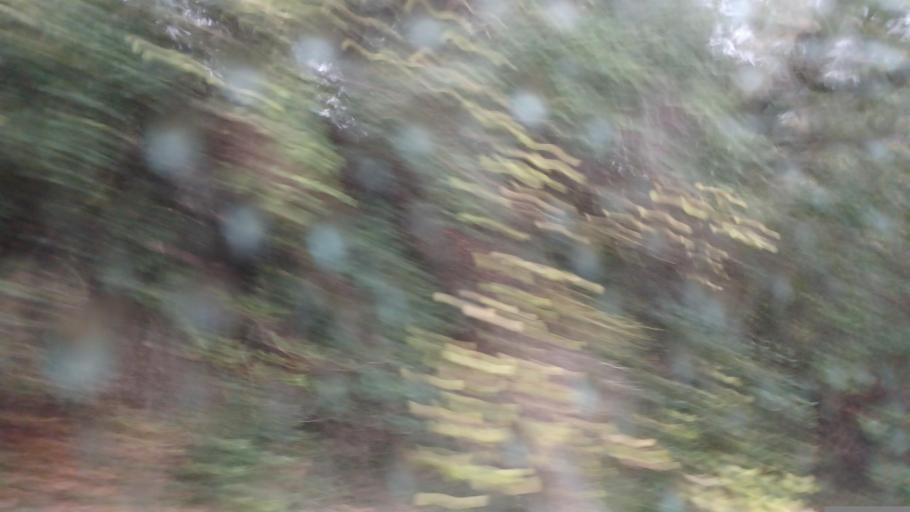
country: CY
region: Pafos
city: Mesogi
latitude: 34.8713
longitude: 32.5410
